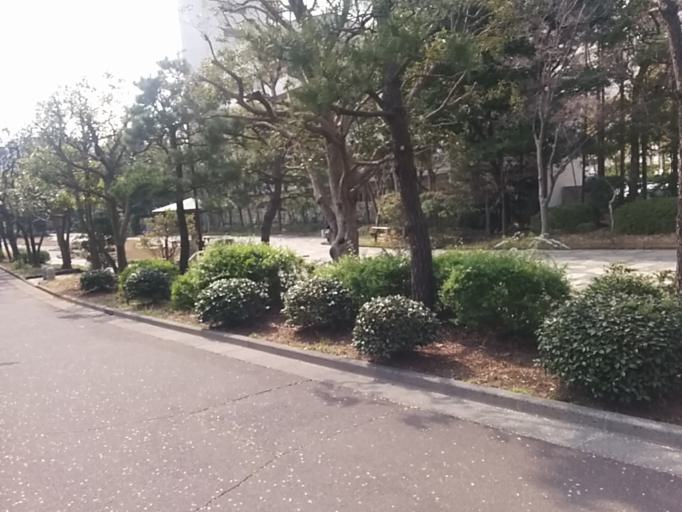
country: JP
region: Tokyo
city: Urayasu
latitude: 35.6516
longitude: 139.8577
